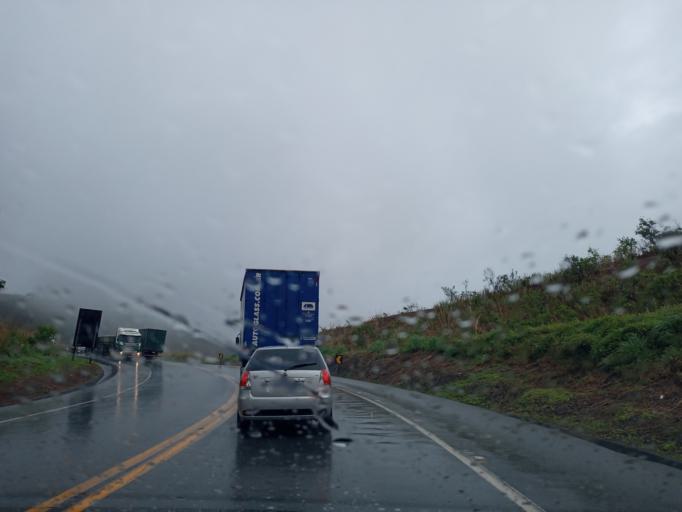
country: BR
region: Minas Gerais
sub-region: Luz
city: Luz
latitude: -19.7174
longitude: -45.8816
